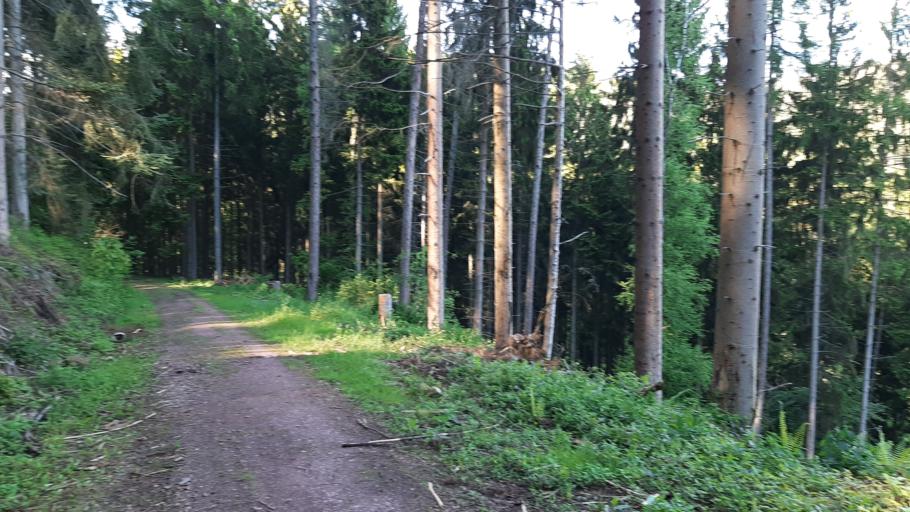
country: DE
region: Rheinland-Pfalz
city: Trierweiler
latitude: 49.7443
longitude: 6.5825
